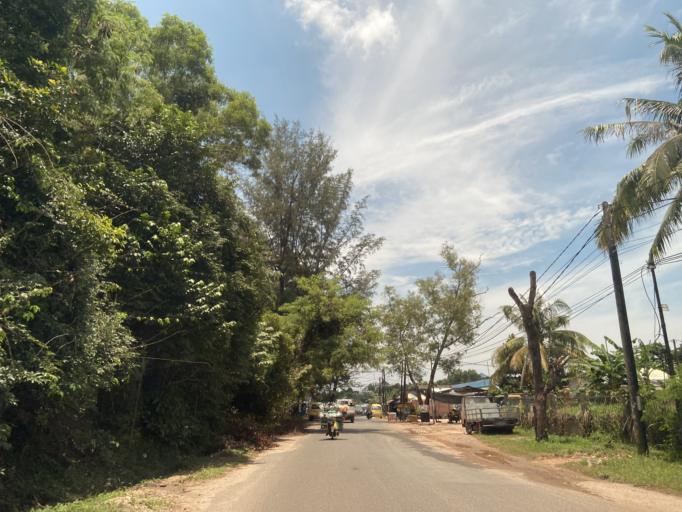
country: SG
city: Singapore
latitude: 1.1600
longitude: 104.0188
